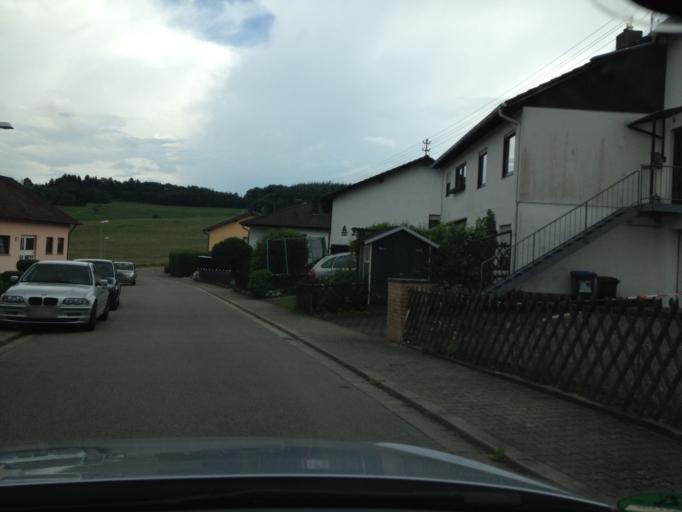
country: DE
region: Rheinland-Pfalz
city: Reichweiler
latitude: 49.5315
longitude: 7.2801
